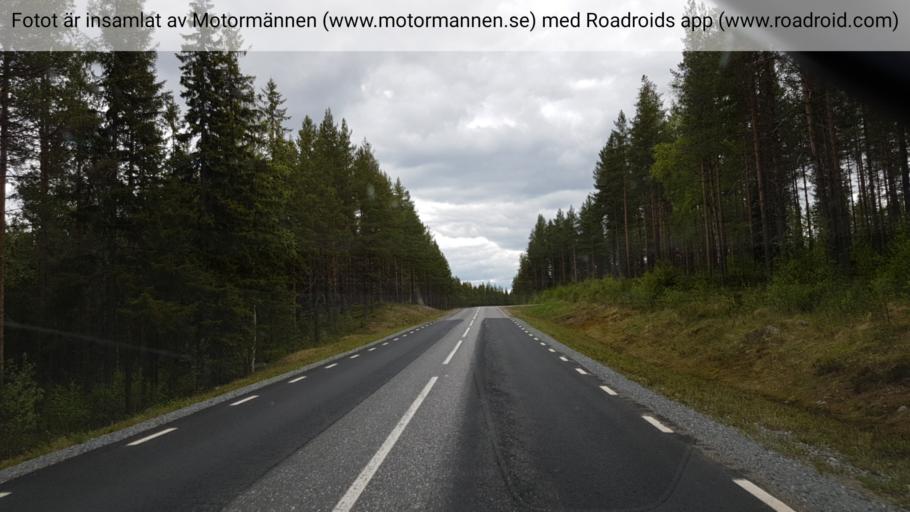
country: SE
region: Vaesterbotten
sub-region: Skelleftea Kommun
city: Langsele
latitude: 64.5966
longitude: 19.9326
